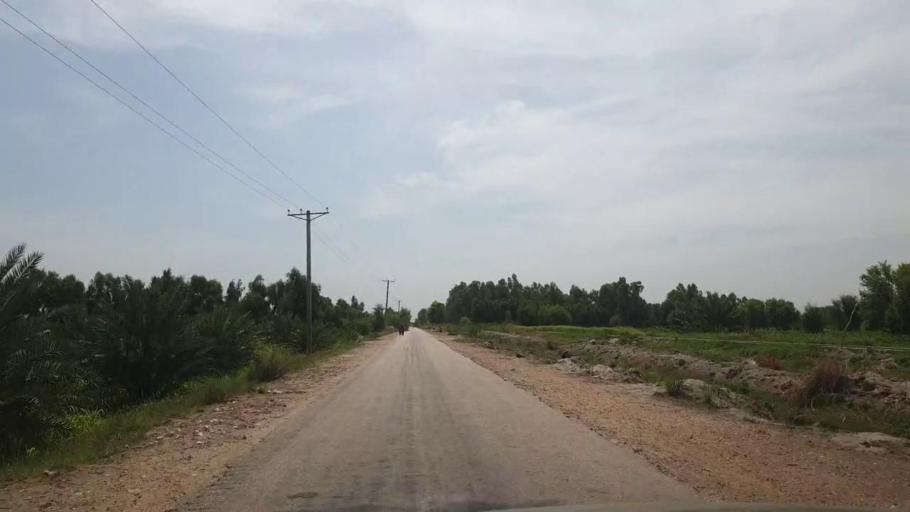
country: PK
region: Sindh
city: Kot Diji
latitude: 27.1209
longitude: 69.0017
